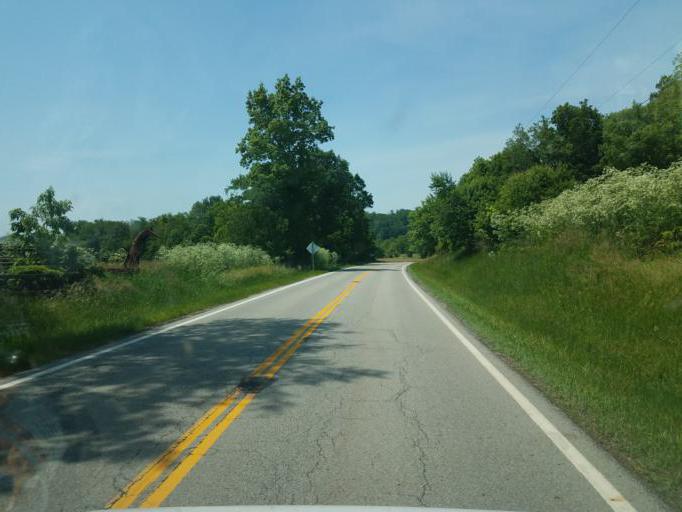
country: US
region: Ohio
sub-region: Ashland County
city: Loudonville
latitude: 40.6806
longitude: -82.2783
